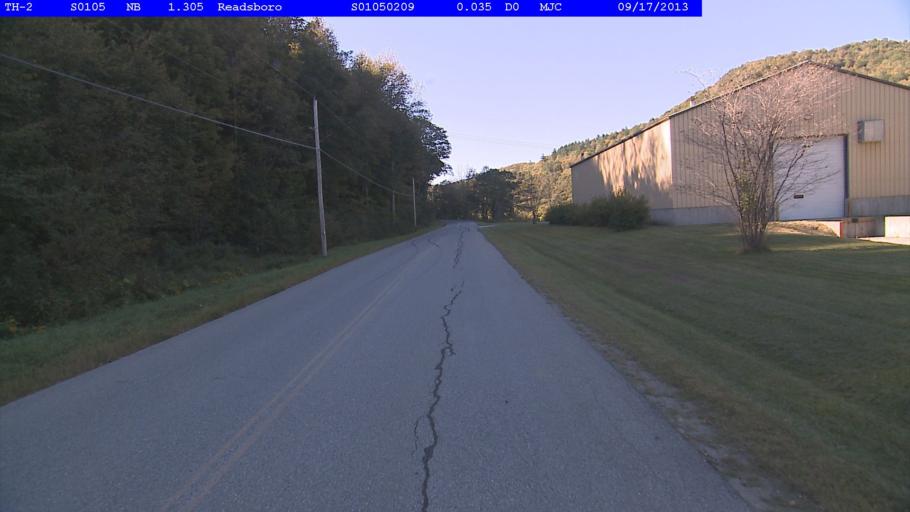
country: US
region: Massachusetts
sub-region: Franklin County
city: Charlemont
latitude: 42.7559
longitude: -72.9302
